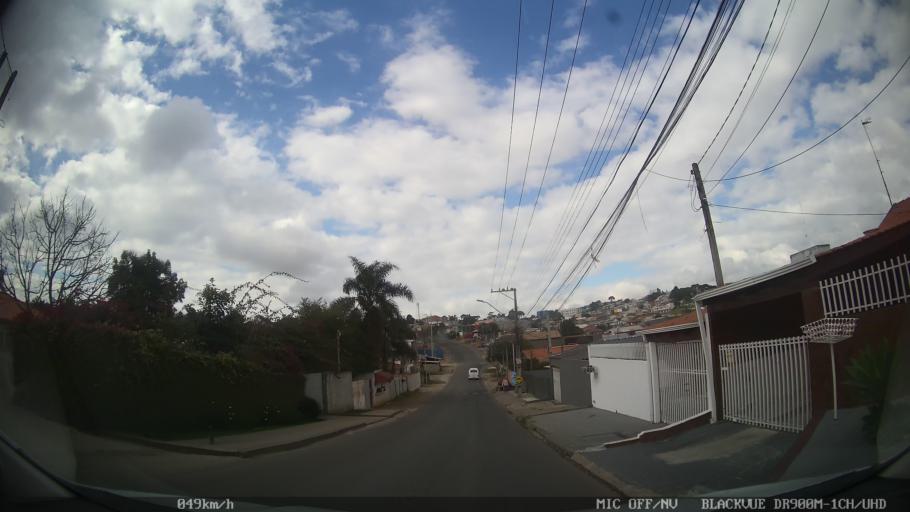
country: BR
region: Parana
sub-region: Colombo
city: Colombo
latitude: -25.3617
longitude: -49.1972
